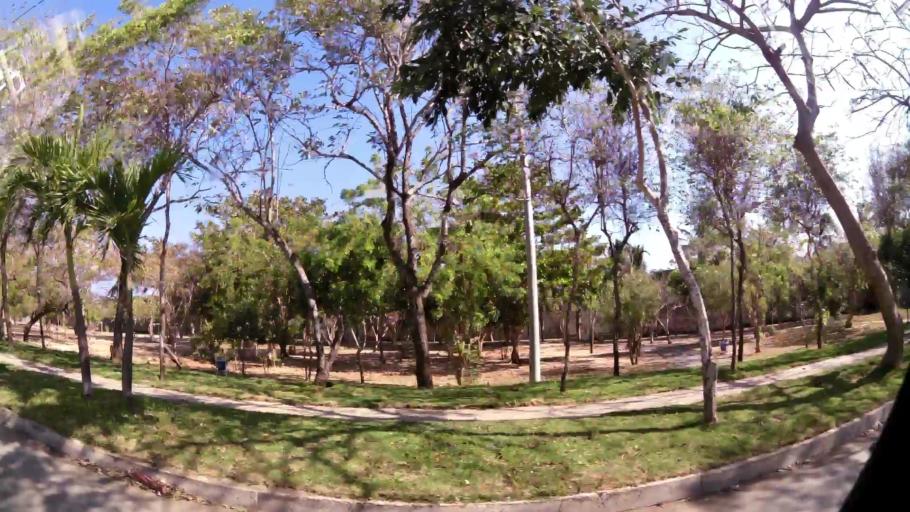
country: CO
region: Atlantico
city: Barranquilla
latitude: 11.0241
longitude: -74.8098
